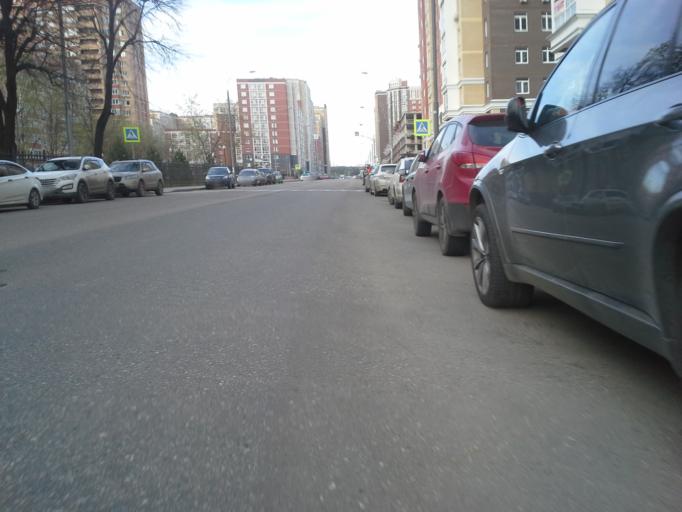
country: RU
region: Moskovskaya
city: Kommunarka
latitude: 55.5671
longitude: 37.4859
